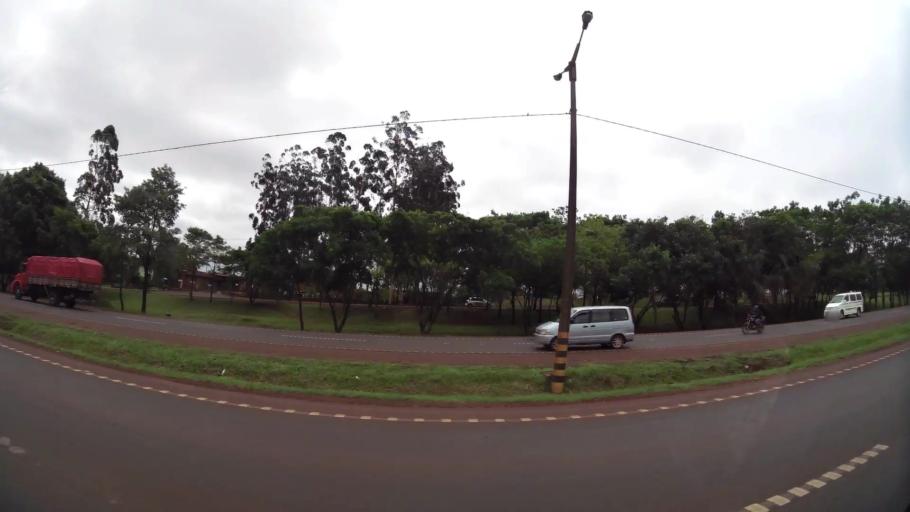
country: PY
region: Alto Parana
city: Ciudad del Este
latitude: -25.4972
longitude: -54.6691
